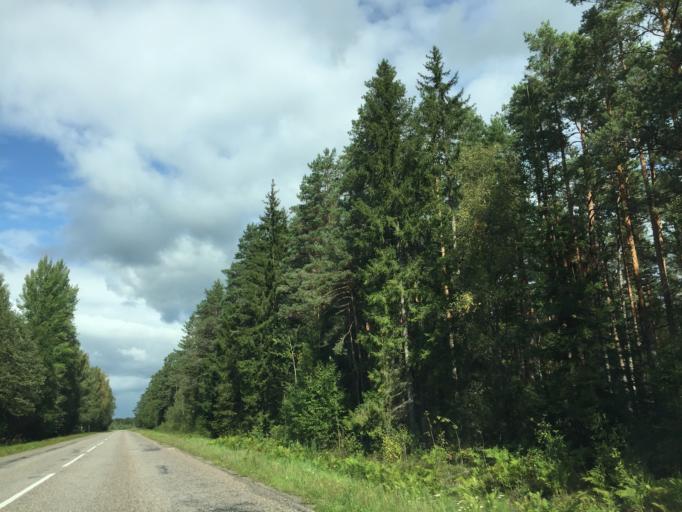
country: LV
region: Pargaujas
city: Stalbe
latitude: 57.4469
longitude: 24.9233
